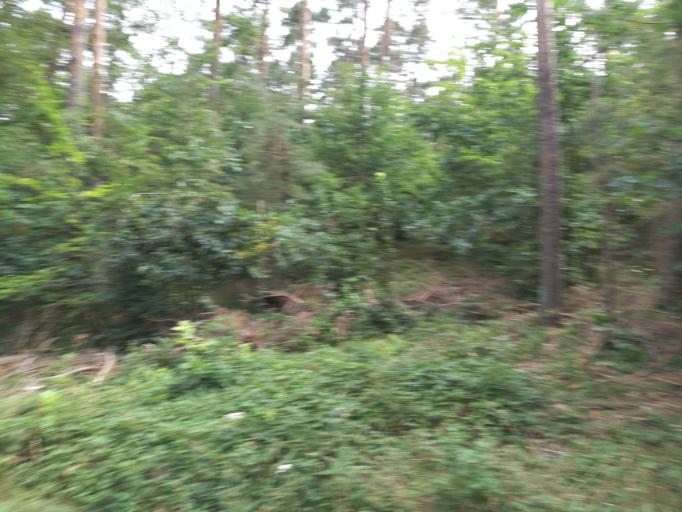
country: DE
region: Bavaria
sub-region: Regierungsbezirk Mittelfranken
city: Seukendorf
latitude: 49.4729
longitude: 10.9059
